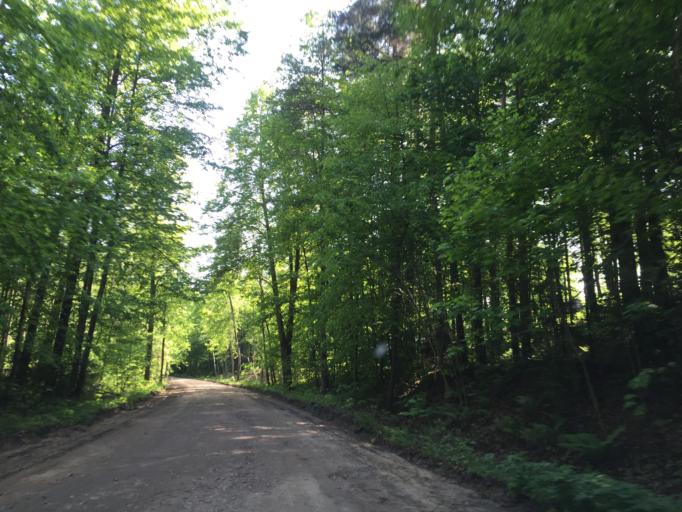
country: LV
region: Ikskile
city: Ikskile
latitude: 56.8283
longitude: 24.4315
